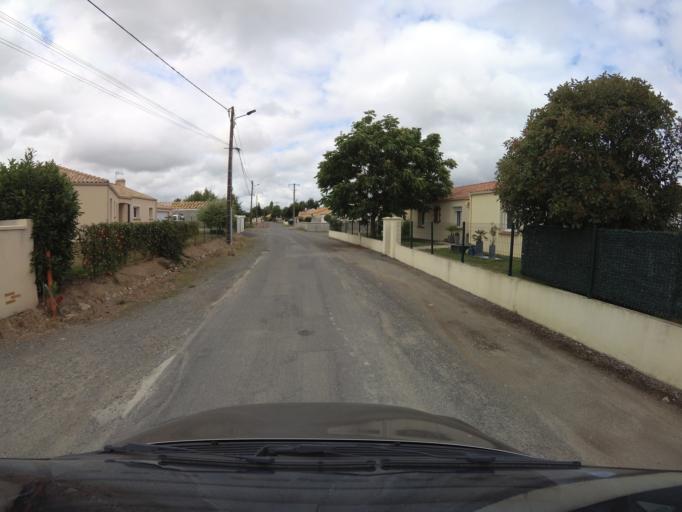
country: FR
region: Pays de la Loire
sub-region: Departement de la Loire-Atlantique
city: La Limouziniere
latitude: 47.0169
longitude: -1.5607
